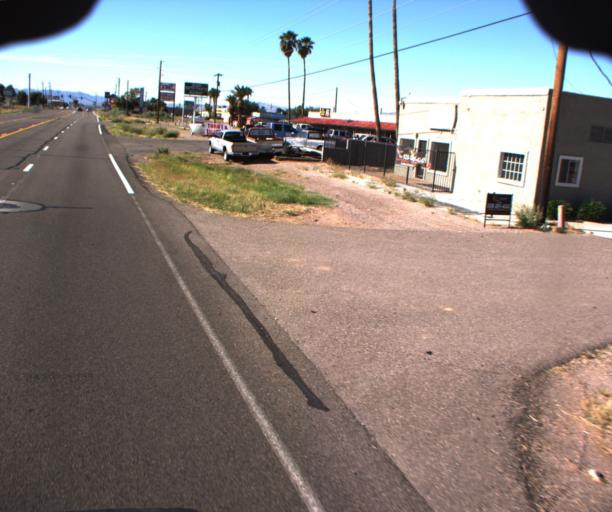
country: US
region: Arizona
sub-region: Mohave County
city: Willow Valley
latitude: 34.9125
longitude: -114.5979
